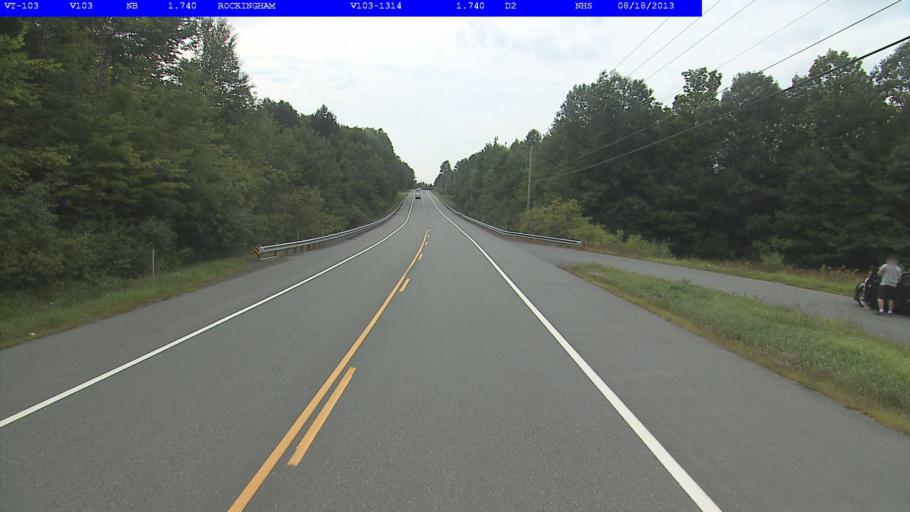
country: US
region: Vermont
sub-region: Windham County
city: Rockingham
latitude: 43.1908
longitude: -72.4881
